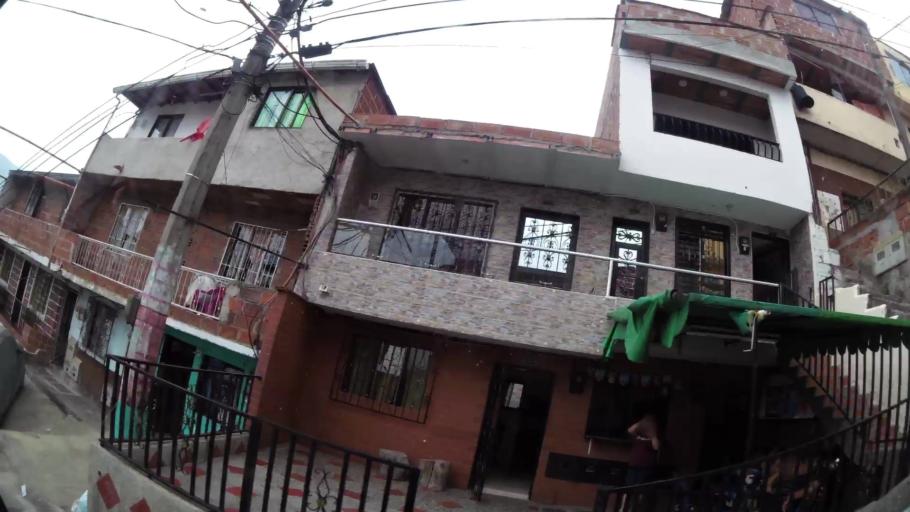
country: CO
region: Antioquia
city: Medellin
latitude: 6.2911
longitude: -75.5508
